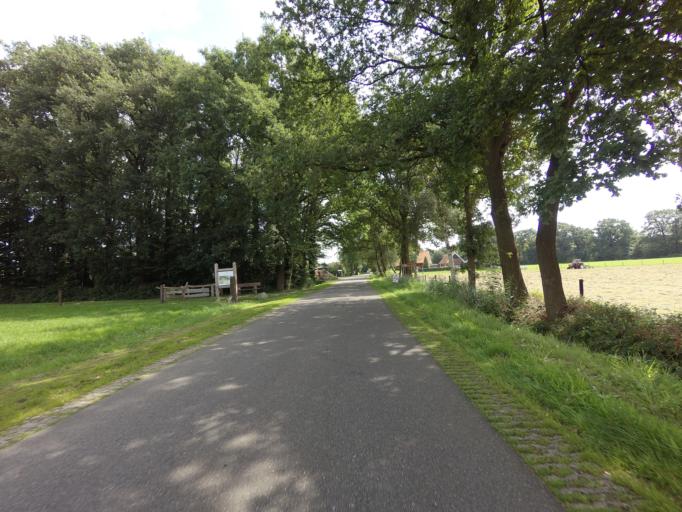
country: DE
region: Lower Saxony
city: Getelo
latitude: 52.4096
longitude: 6.8675
